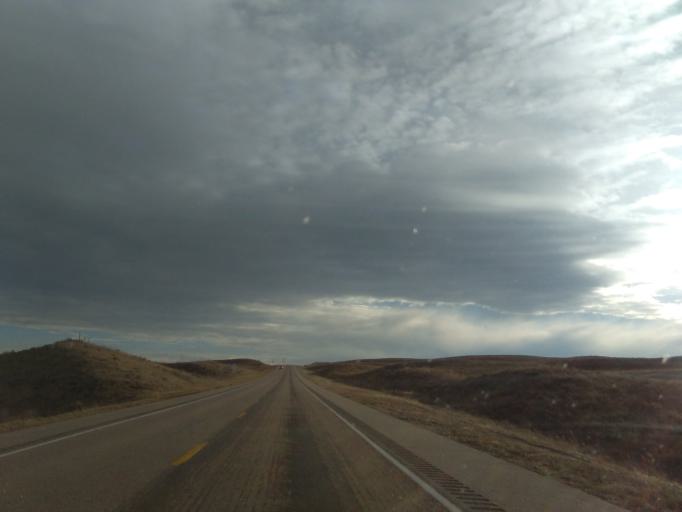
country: US
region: Nebraska
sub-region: Morrill County
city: Bridgeport
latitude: 41.5955
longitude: -102.9839
